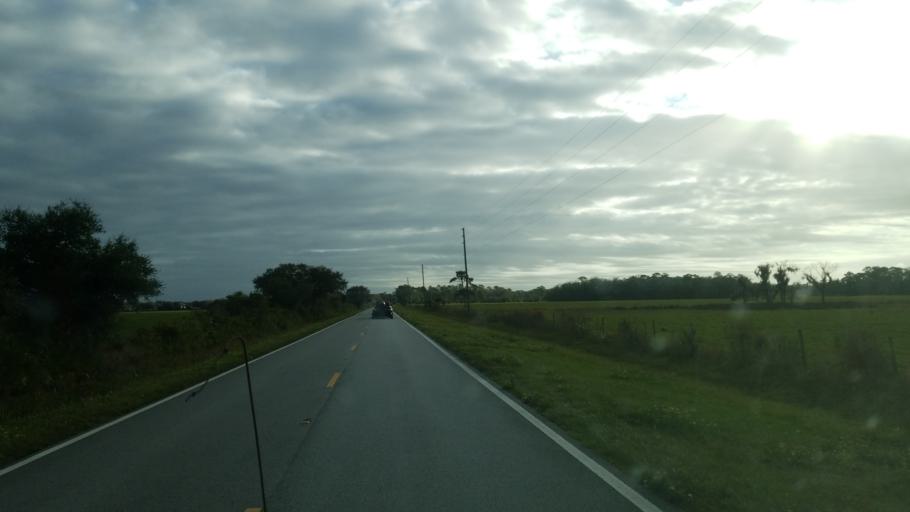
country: US
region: Florida
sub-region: Osceola County
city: Poinciana
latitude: 27.9707
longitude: -81.3896
